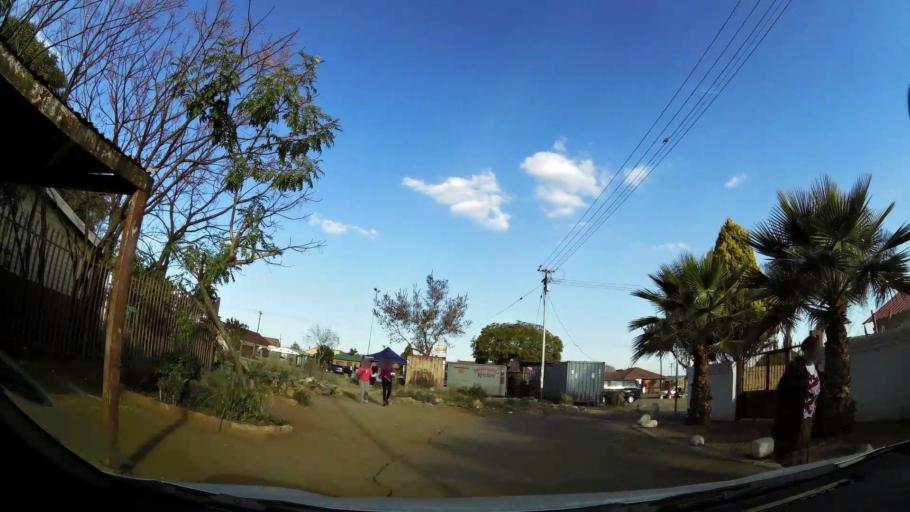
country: ZA
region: Gauteng
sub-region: City of Tshwane Metropolitan Municipality
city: Cullinan
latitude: -25.7073
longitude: 28.3856
